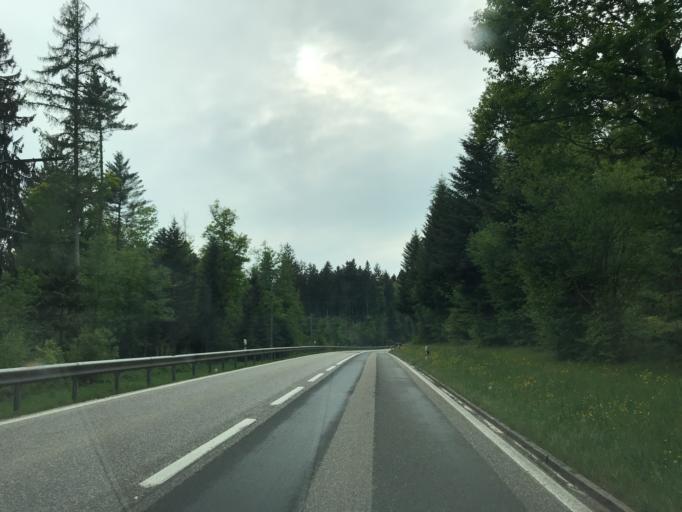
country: CH
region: Bern
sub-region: Oberaargau
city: Aarwangen
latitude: 47.2499
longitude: 7.7349
